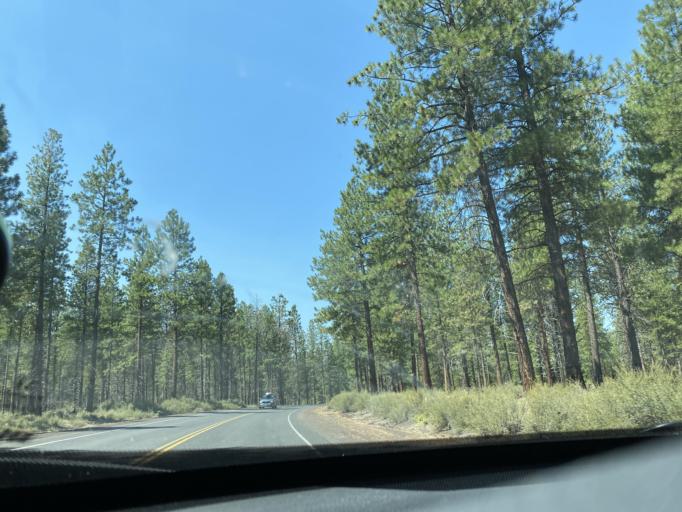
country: US
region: Oregon
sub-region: Deschutes County
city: Sunriver
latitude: 43.8889
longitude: -121.3956
